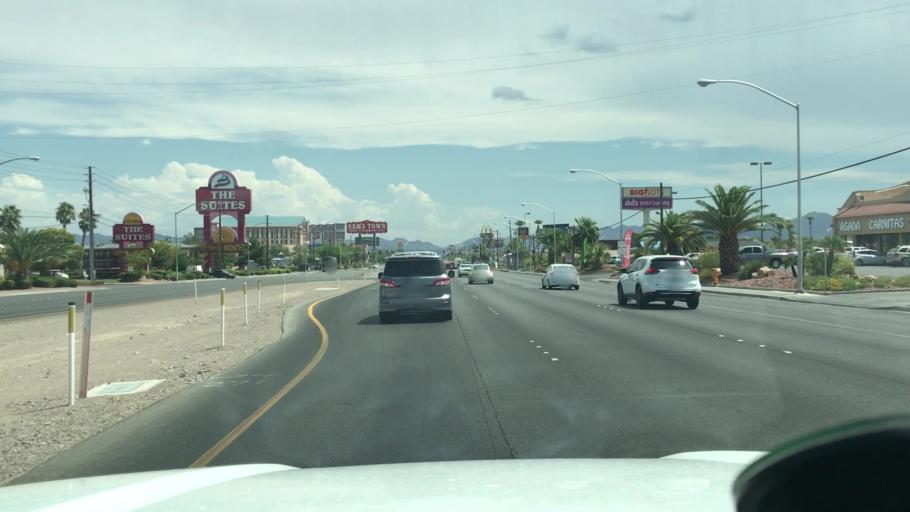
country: US
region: Nevada
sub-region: Clark County
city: Whitney
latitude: 36.1171
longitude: -115.0694
